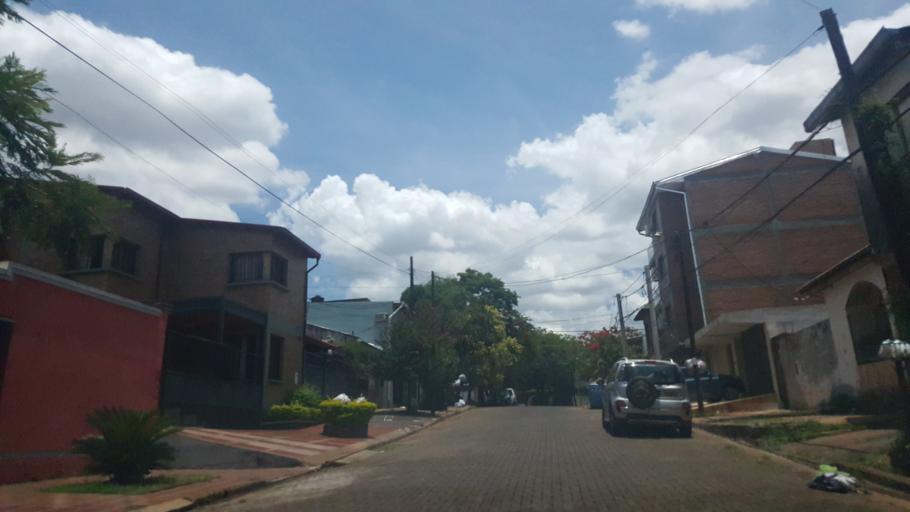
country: AR
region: Misiones
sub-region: Departamento de Capital
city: Posadas
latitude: -27.3628
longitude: -55.9028
